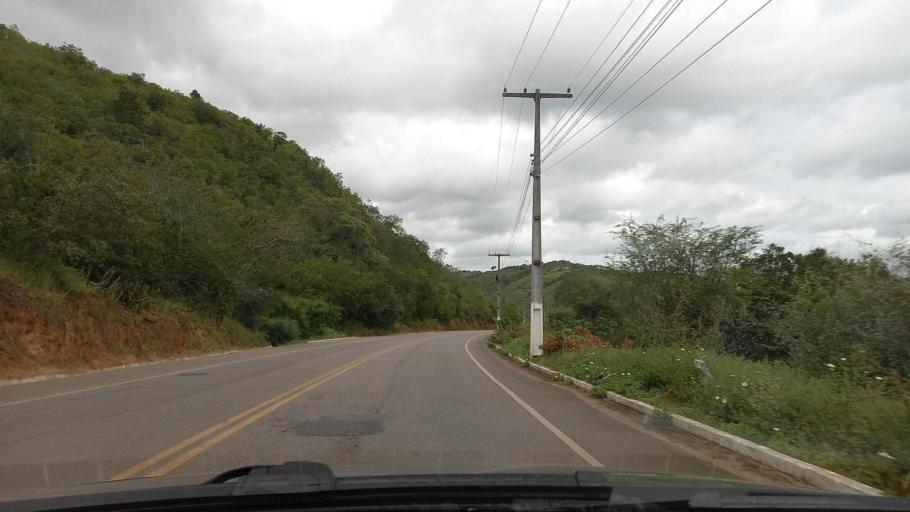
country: BR
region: Sergipe
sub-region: Caninde De Sao Francisco
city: Caninde de Sao Francisco
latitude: -9.6400
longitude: -37.7746
